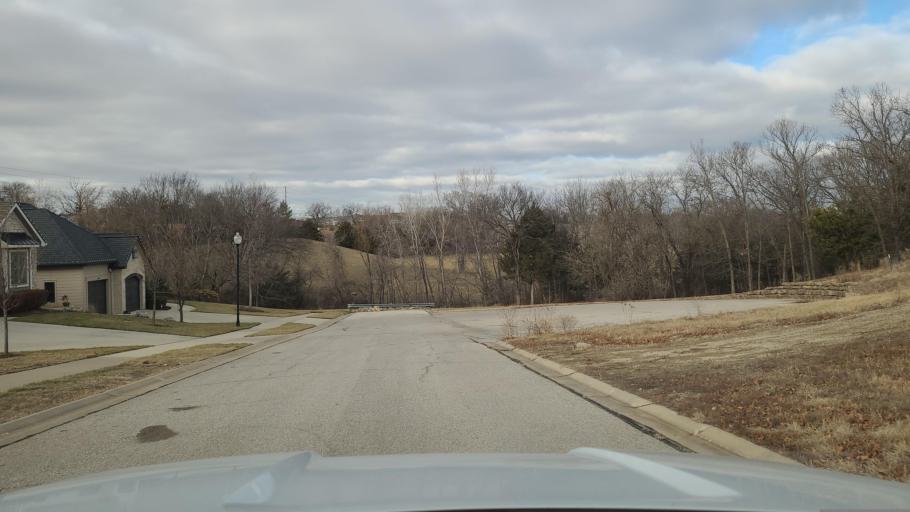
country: US
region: Kansas
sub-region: Douglas County
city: Lawrence
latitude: 38.9818
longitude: -95.2869
